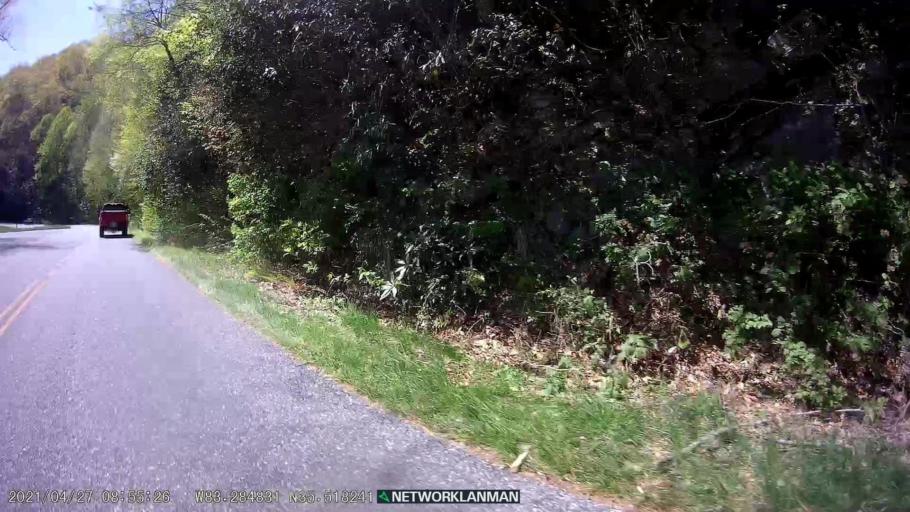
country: US
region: North Carolina
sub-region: Swain County
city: Cherokee
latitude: 35.5179
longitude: -83.2848
